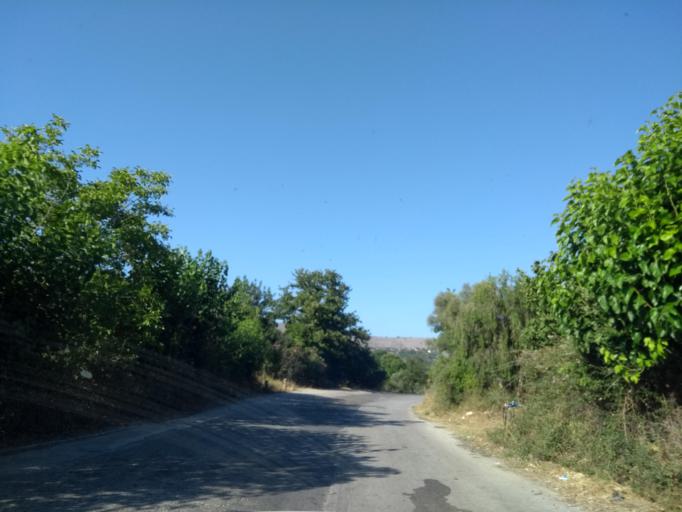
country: GR
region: Crete
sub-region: Nomos Chanias
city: Georgioupolis
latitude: 35.3654
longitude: 24.2230
